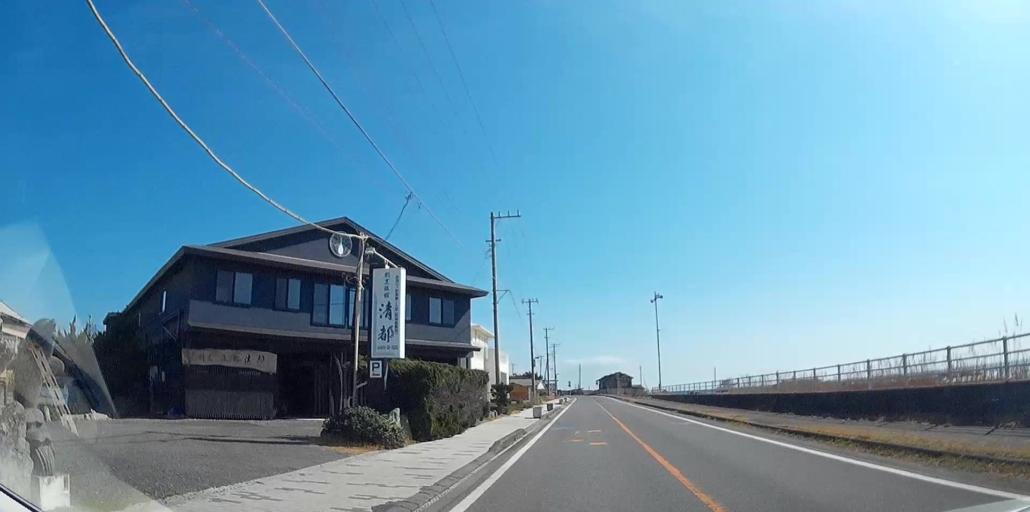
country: JP
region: Chiba
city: Tateyama
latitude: 34.9057
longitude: 139.8700
